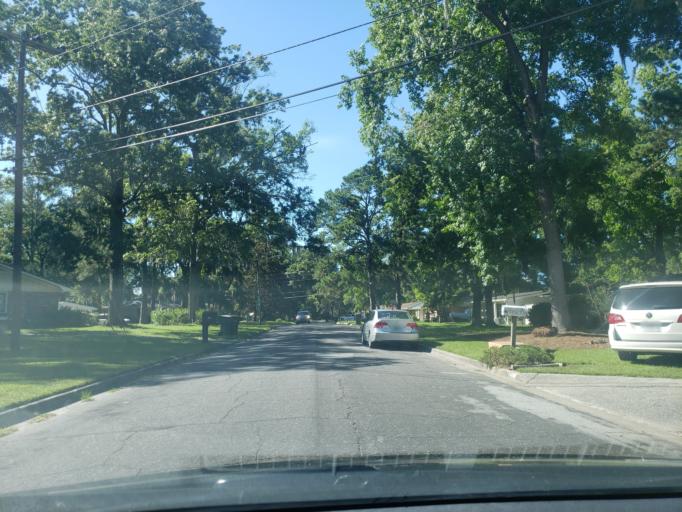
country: US
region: Georgia
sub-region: Chatham County
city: Montgomery
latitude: 31.9879
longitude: -81.1370
